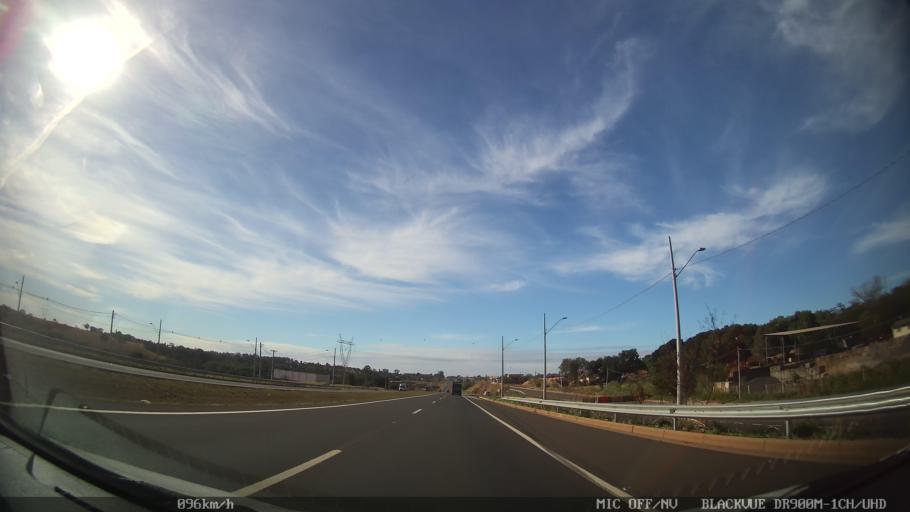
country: BR
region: Sao Paulo
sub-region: Sao Jose Do Rio Preto
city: Sao Jose do Rio Preto
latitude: -20.7586
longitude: -49.3449
